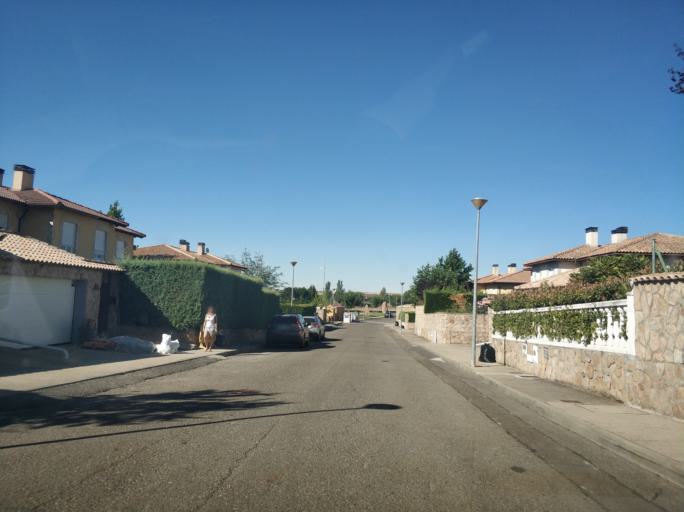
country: ES
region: Castille and Leon
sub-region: Provincia de Salamanca
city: Santa Marta de Tormes
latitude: 40.9420
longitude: -5.6207
